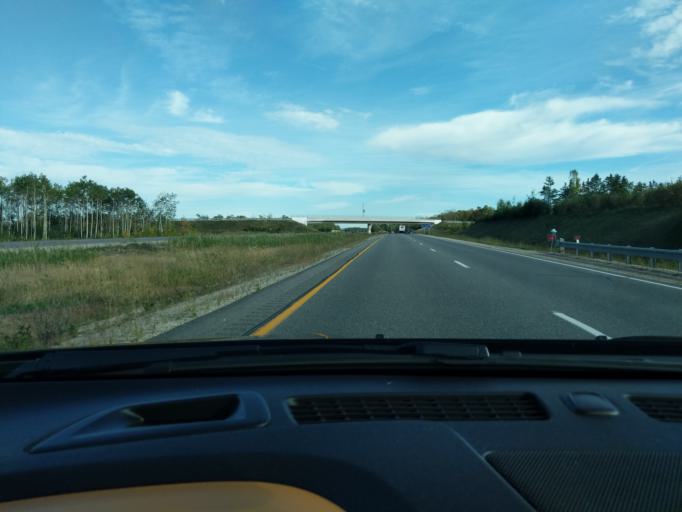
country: CA
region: Ontario
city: Collingwood
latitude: 44.4715
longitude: -80.1438
